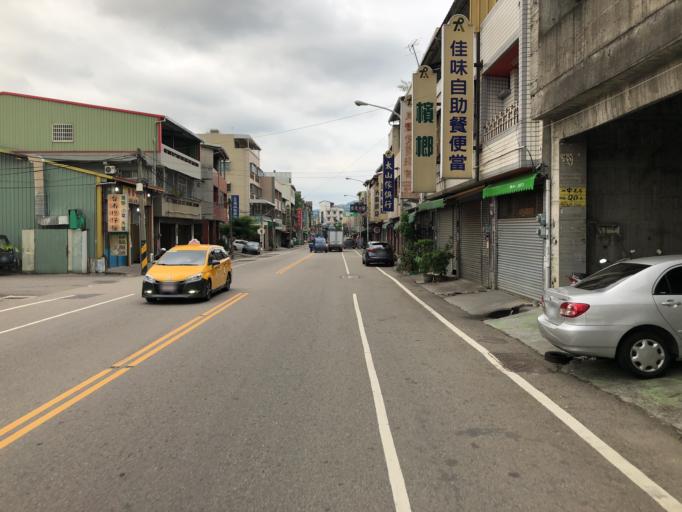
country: TW
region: Taiwan
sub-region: Taichung City
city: Taichung
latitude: 24.1100
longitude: 120.7301
